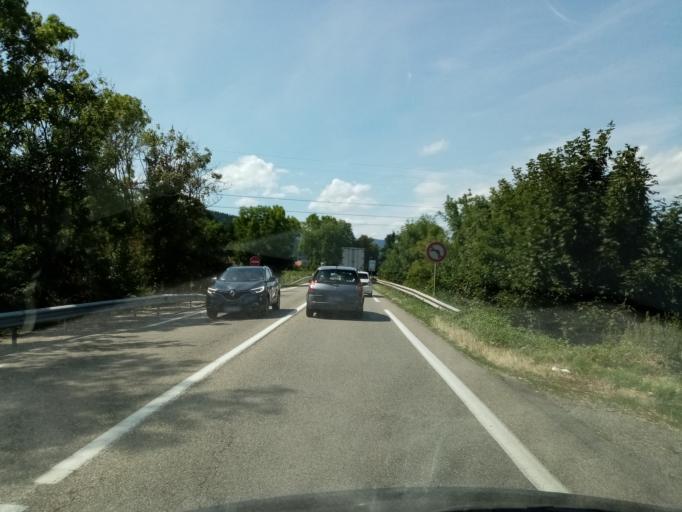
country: FR
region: Alsace
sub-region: Departement du Bas-Rhin
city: Chatenois
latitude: 48.2722
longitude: 7.4142
